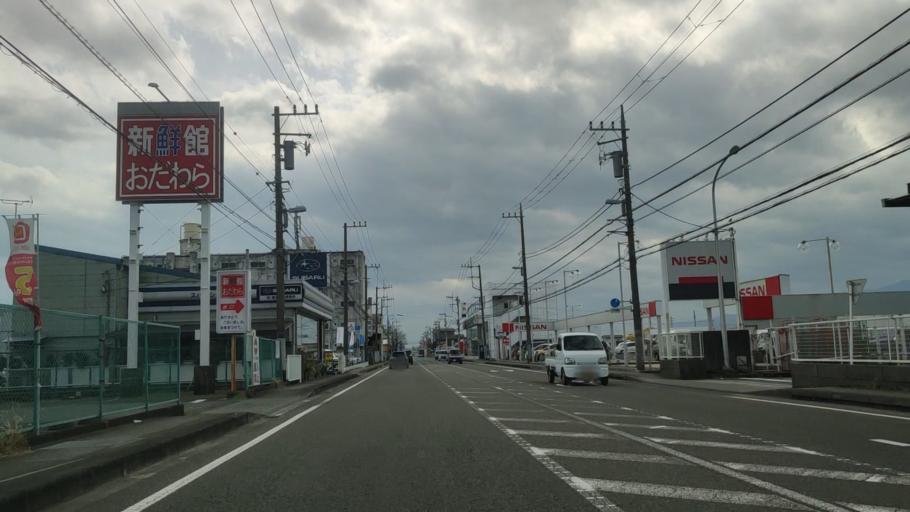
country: JP
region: Kanagawa
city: Odawara
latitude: 35.3039
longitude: 139.1664
